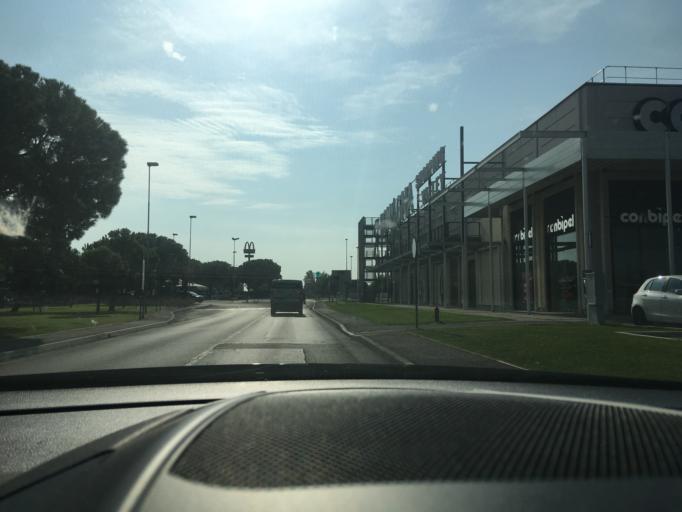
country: IT
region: Emilia-Romagna
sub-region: Forli-Cesena
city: Gatteo a Mare
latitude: 44.1574
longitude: 12.4312
